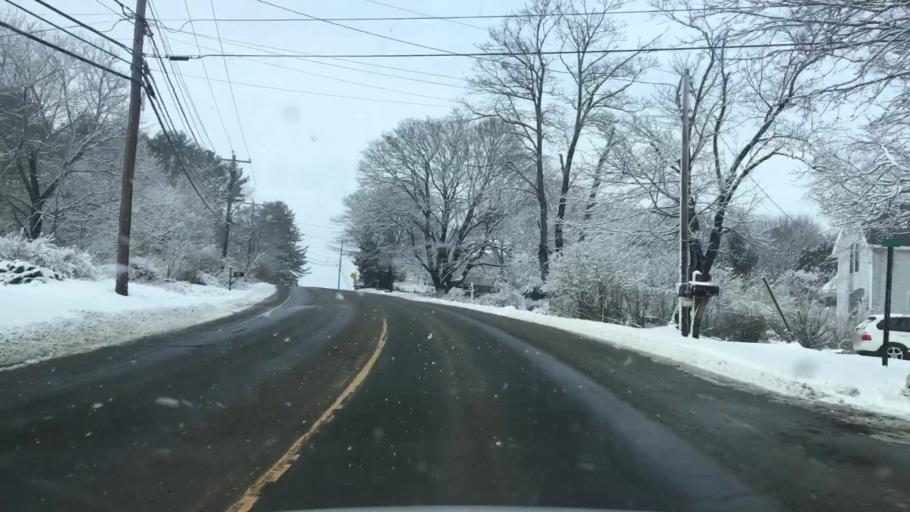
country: US
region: Maine
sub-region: Knox County
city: Rockland
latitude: 44.0857
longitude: -69.1065
